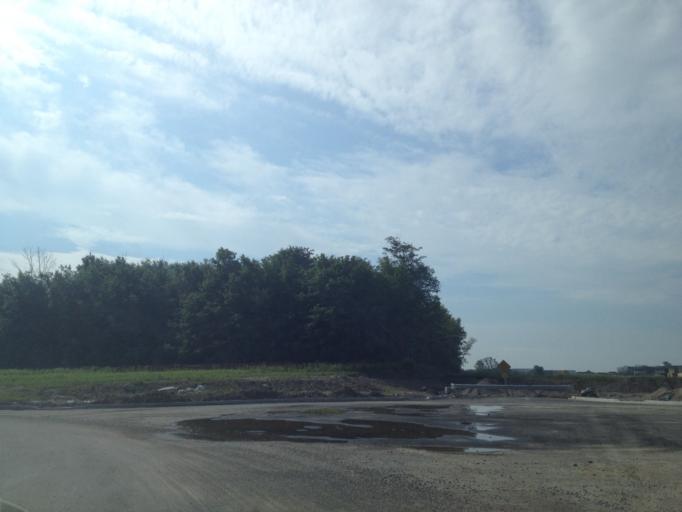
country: CA
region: Ontario
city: London
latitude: 43.0237
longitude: -81.3332
